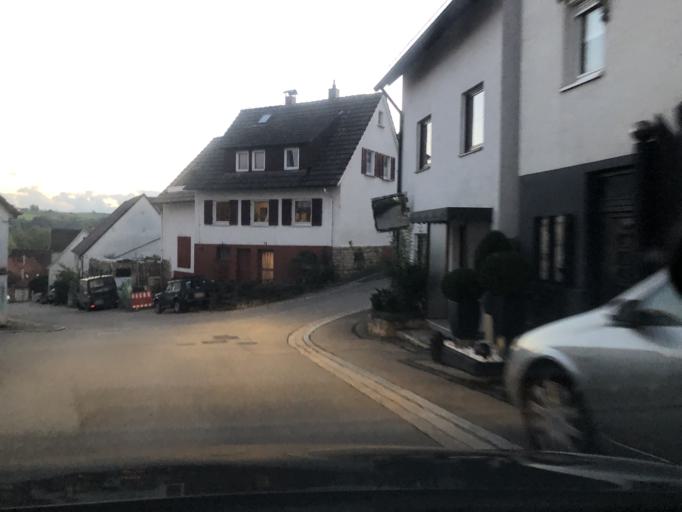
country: DE
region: Baden-Wuerttemberg
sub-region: Regierungsbezirk Stuttgart
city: Grossbettlingen
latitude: 48.6198
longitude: 9.3105
